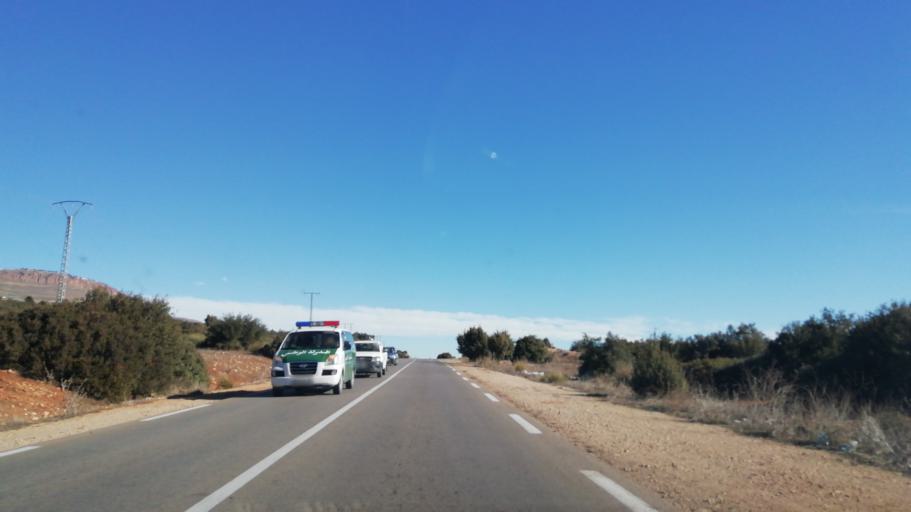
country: DZ
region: Tlemcen
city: Sebdou
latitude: 34.7186
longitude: -1.2020
